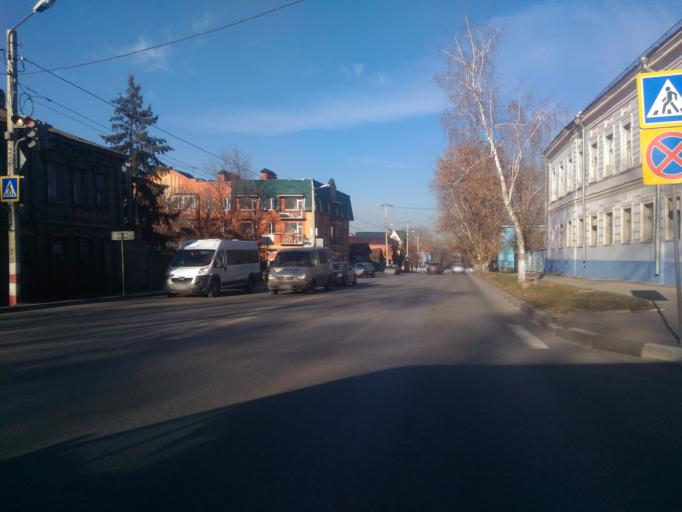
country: RU
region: Ulyanovsk
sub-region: Ulyanovskiy Rayon
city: Ulyanovsk
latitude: 54.3107
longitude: 48.3787
